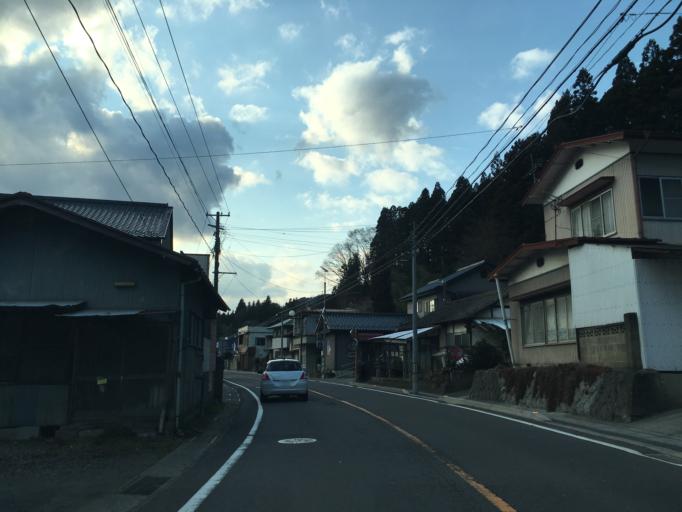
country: JP
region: Fukushima
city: Ishikawa
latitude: 37.0906
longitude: 140.5559
